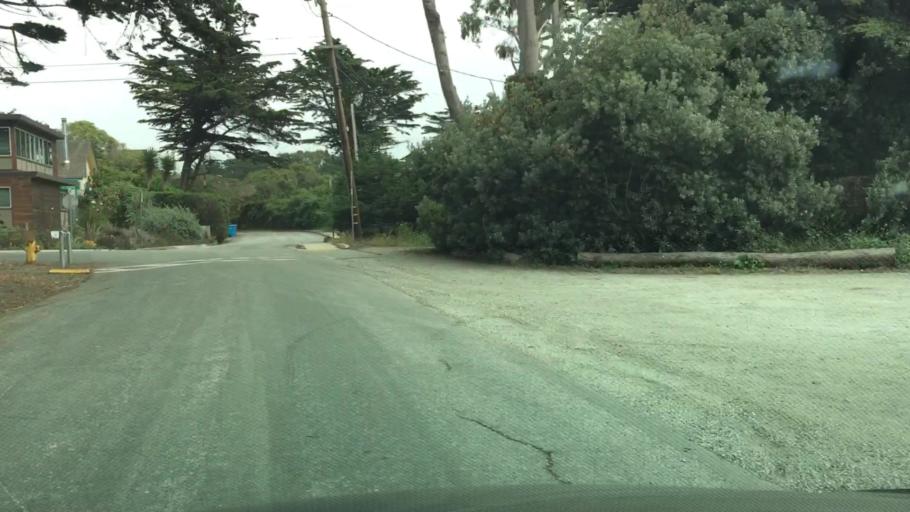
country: US
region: California
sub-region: San Mateo County
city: Moss Beach
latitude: 37.5238
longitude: -122.5163
